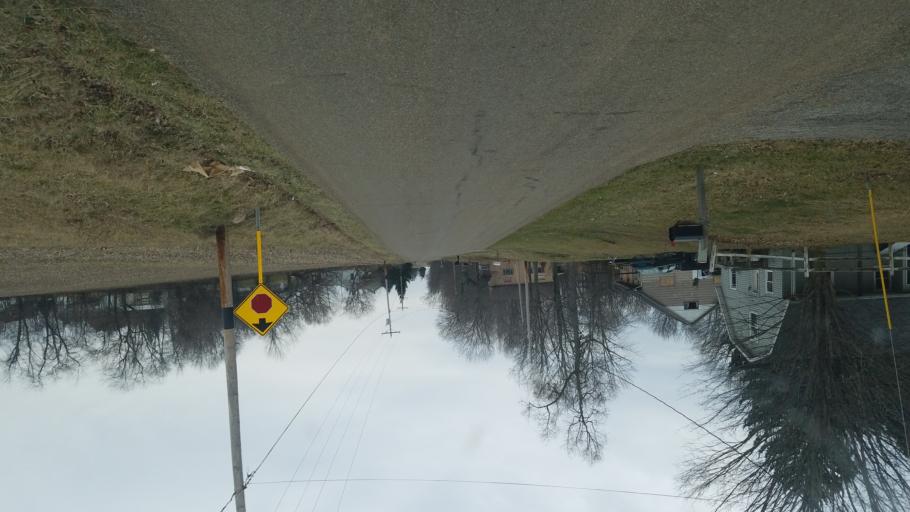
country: US
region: Ohio
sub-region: Richland County
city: Lincoln Heights
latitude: 40.7416
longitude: -82.3940
